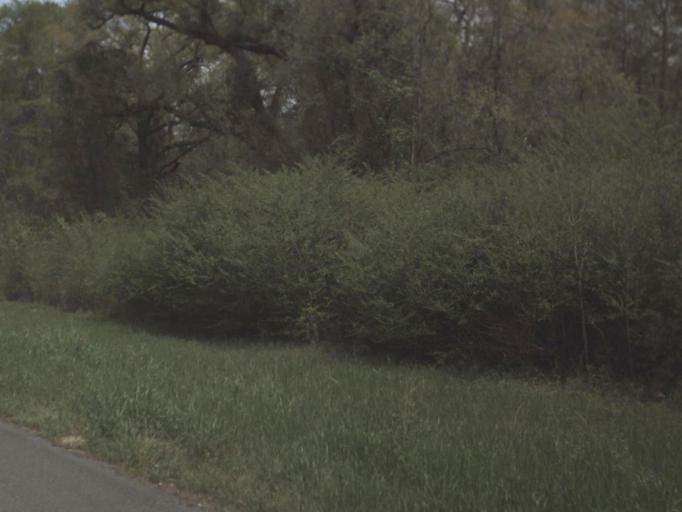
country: US
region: Florida
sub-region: Jackson County
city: Graceville
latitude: 30.9180
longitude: -85.4294
